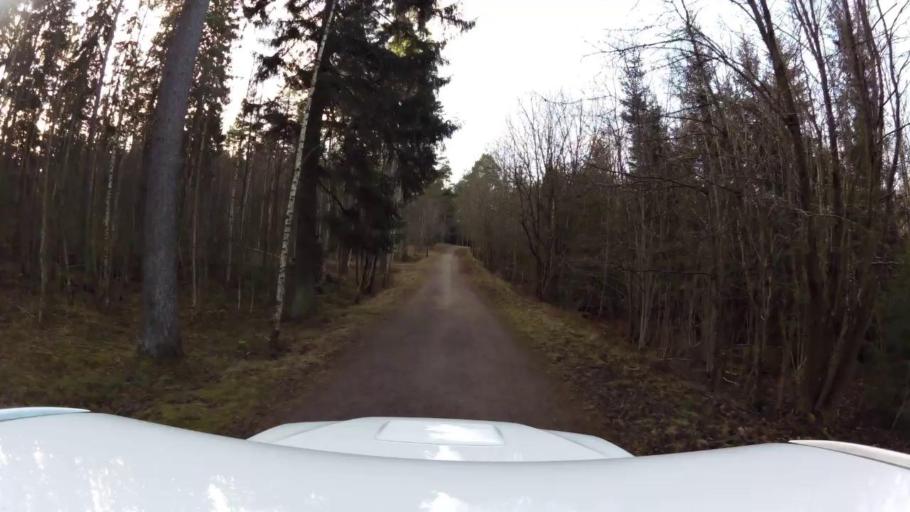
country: SE
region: OEstergoetland
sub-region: Linkopings Kommun
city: Linkoping
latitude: 58.3993
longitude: 15.5985
